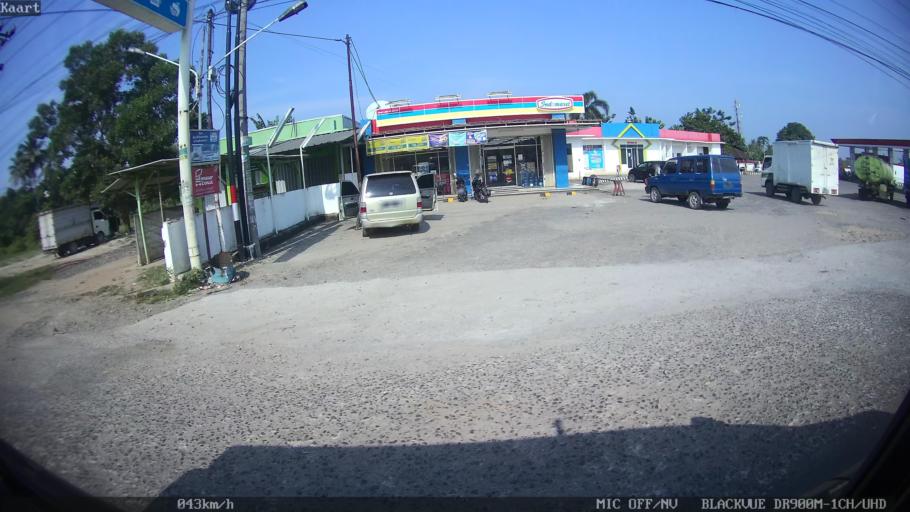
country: ID
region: Lampung
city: Natar
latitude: -5.2796
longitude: 105.1883
